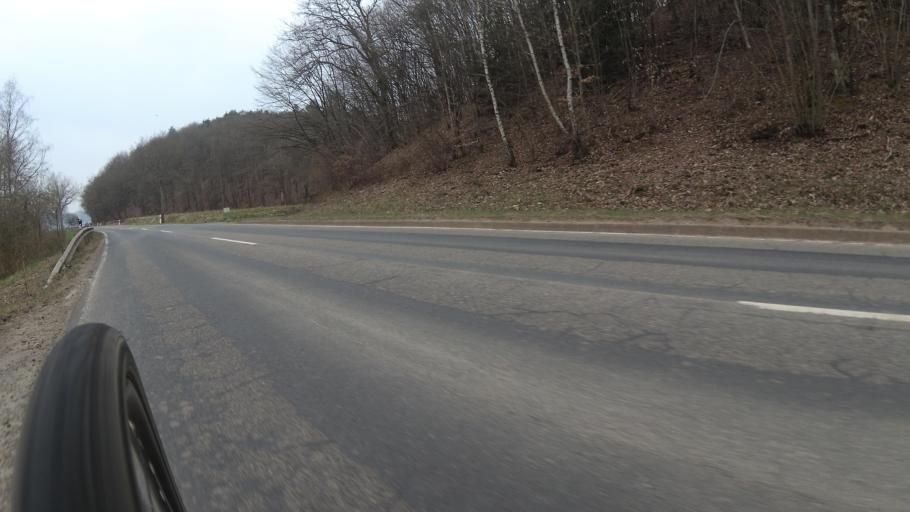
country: DE
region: Rheinland-Pfalz
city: Dienstweiler
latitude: 49.6318
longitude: 7.1933
